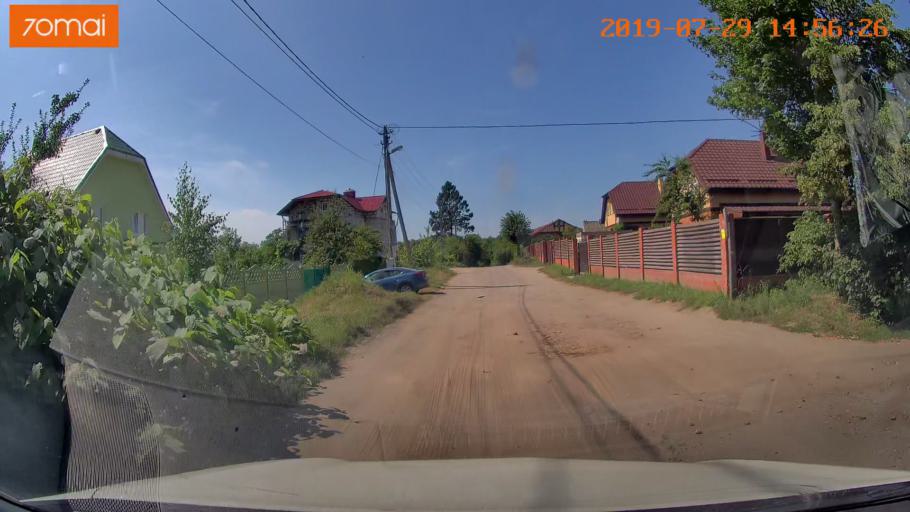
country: RU
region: Kaliningrad
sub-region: Gorod Kaliningrad
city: Baltiysk
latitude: 54.6800
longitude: 19.9205
